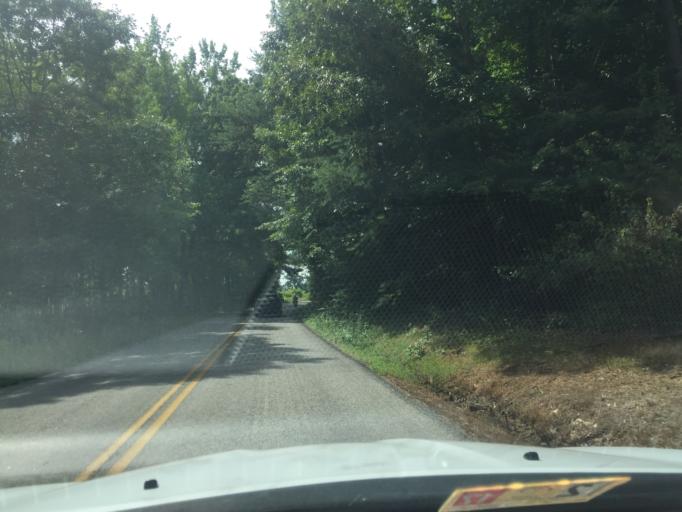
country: US
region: Virginia
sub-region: Charles City County
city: Charles City
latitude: 37.3863
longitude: -77.0118
